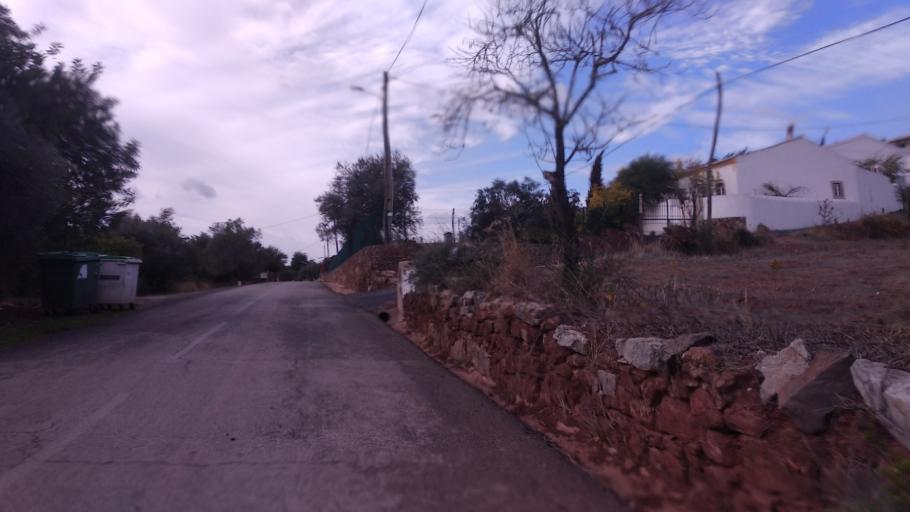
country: PT
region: Faro
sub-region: Sao Bras de Alportel
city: Sao Bras de Alportel
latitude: 37.1752
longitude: -7.9014
